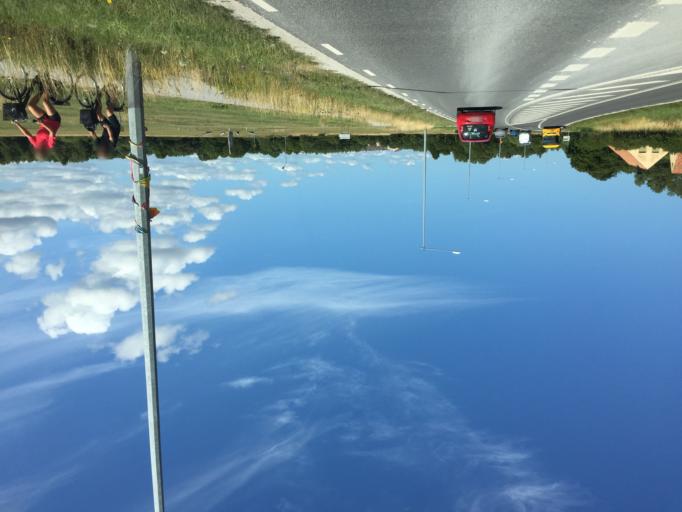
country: SE
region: Gotland
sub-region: Gotland
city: Vibble
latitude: 57.6181
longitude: 18.2722
